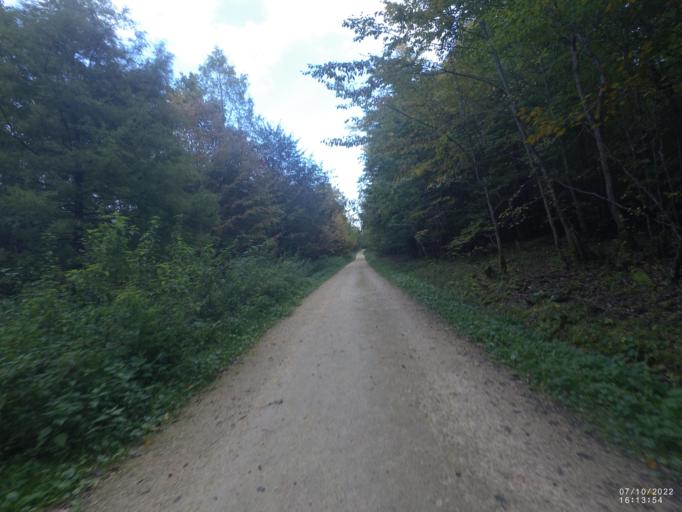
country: DE
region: Baden-Wuerttemberg
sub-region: Regierungsbezirk Stuttgart
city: Eislingen
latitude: 48.7169
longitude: 9.7190
